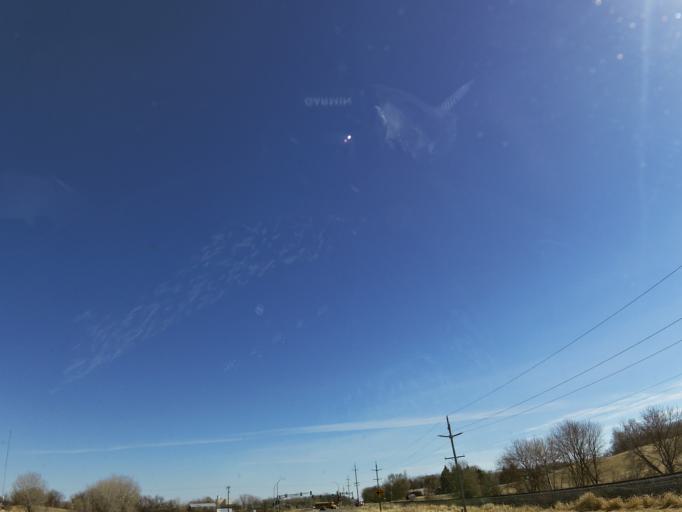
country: US
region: Minnesota
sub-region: Wright County
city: Buffalo
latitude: 45.1922
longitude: -93.8922
